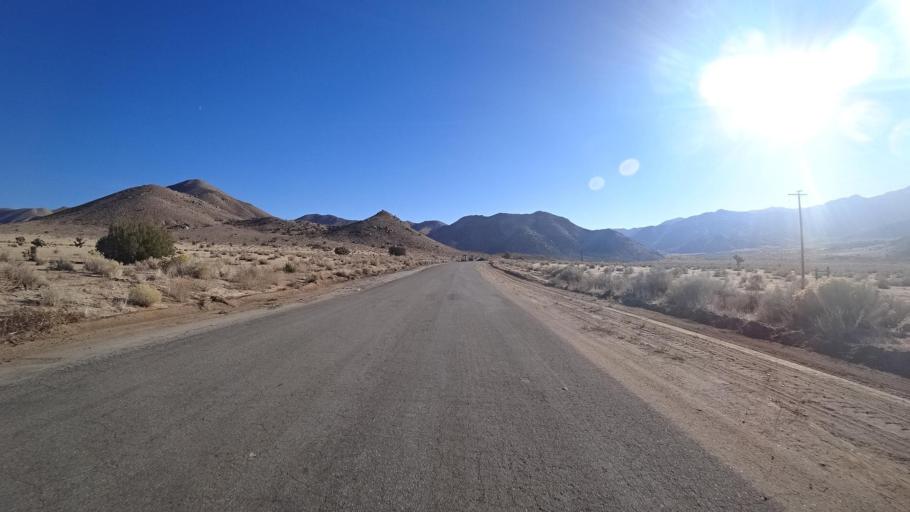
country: US
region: California
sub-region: Kern County
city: Weldon
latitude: 35.5967
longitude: -118.2402
